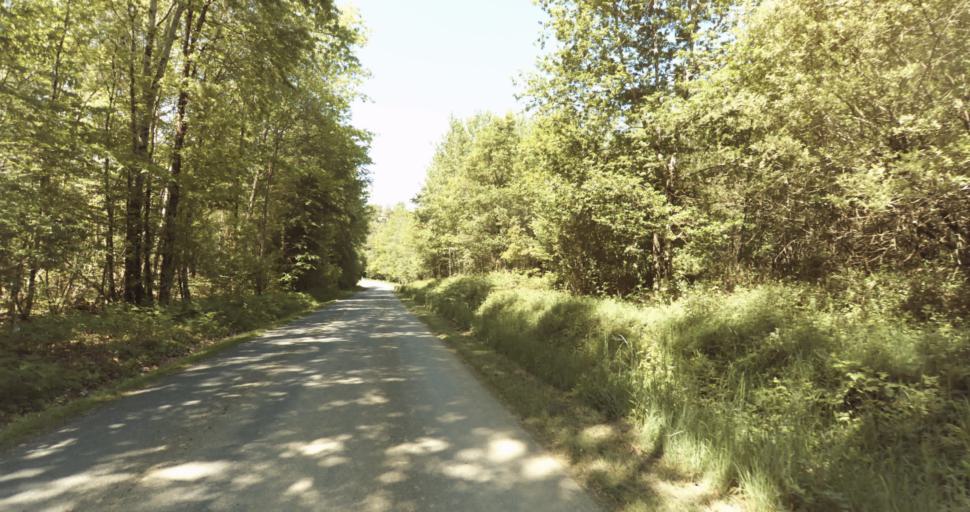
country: FR
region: Limousin
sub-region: Departement de la Haute-Vienne
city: Le Vigen
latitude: 45.7655
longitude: 1.3026
